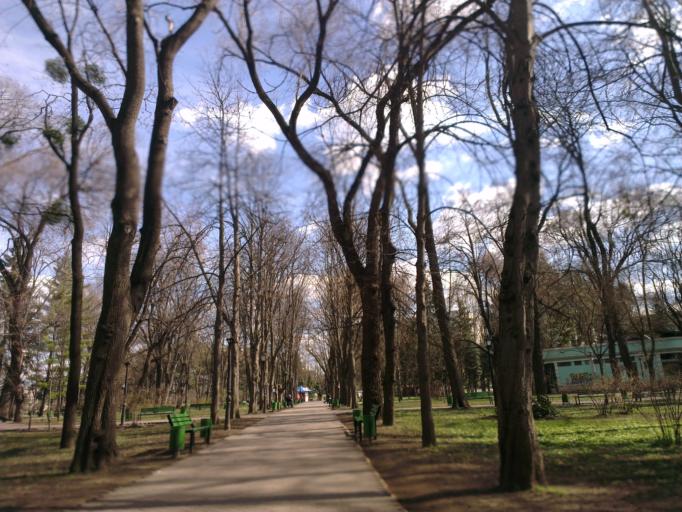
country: MD
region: Chisinau
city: Chisinau
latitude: 47.0246
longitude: 28.8276
